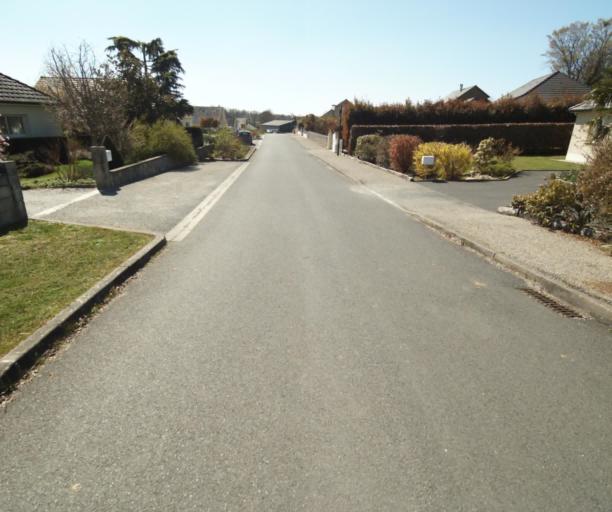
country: FR
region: Limousin
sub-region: Departement de la Correze
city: Saint-Clement
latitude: 45.3398
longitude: 1.6853
